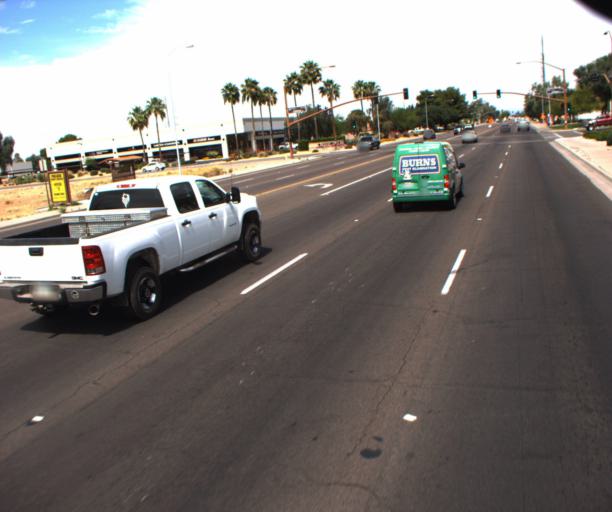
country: US
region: Arizona
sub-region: Maricopa County
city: San Carlos
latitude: 33.3531
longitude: -111.8417
